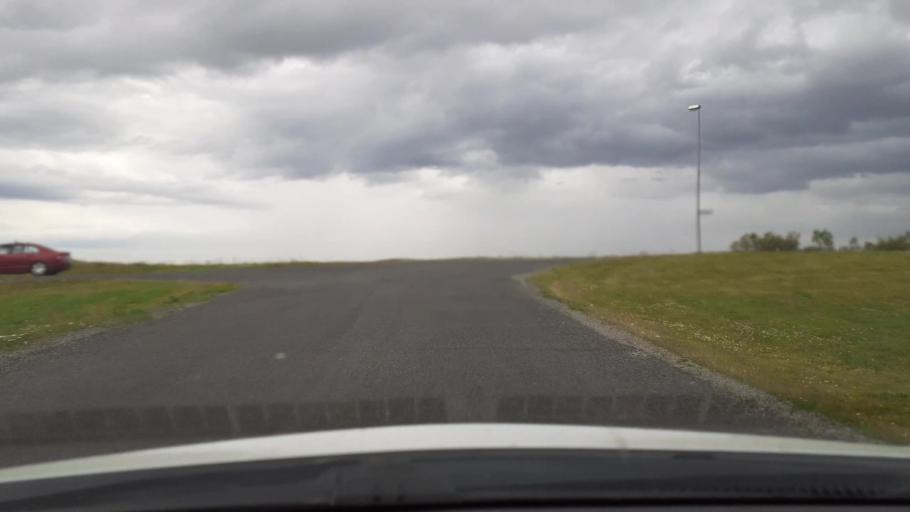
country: IS
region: West
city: Borgarnes
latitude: 64.5652
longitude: -21.7635
